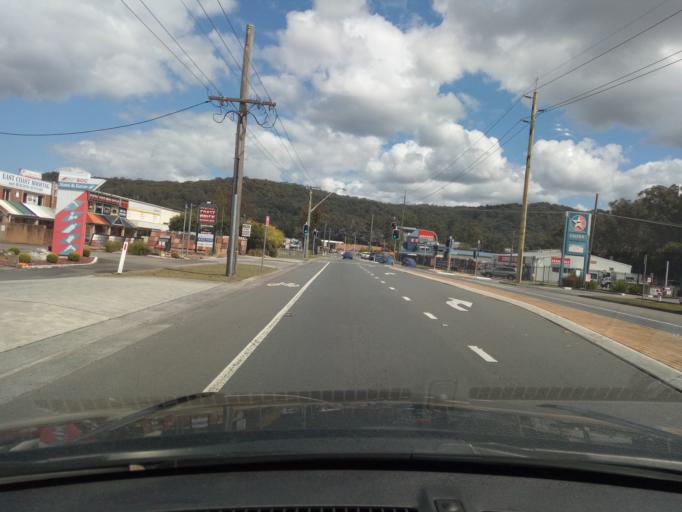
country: AU
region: New South Wales
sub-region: Gosford Shire
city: Gosford
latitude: -33.4169
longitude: 151.3255
